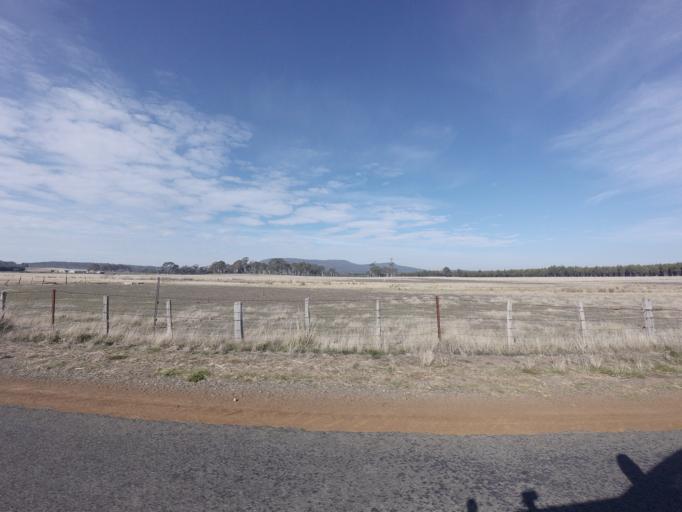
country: AU
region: Tasmania
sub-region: Sorell
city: Sorell
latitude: -42.4403
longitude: 147.4719
